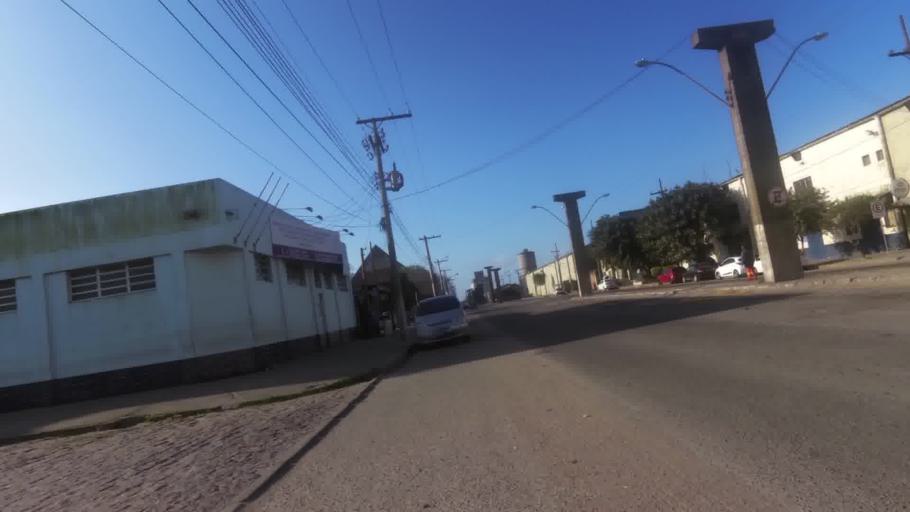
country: BR
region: Rio Grande do Sul
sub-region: Rio Grande
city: Rio Grande
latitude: -32.0432
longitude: -52.0765
